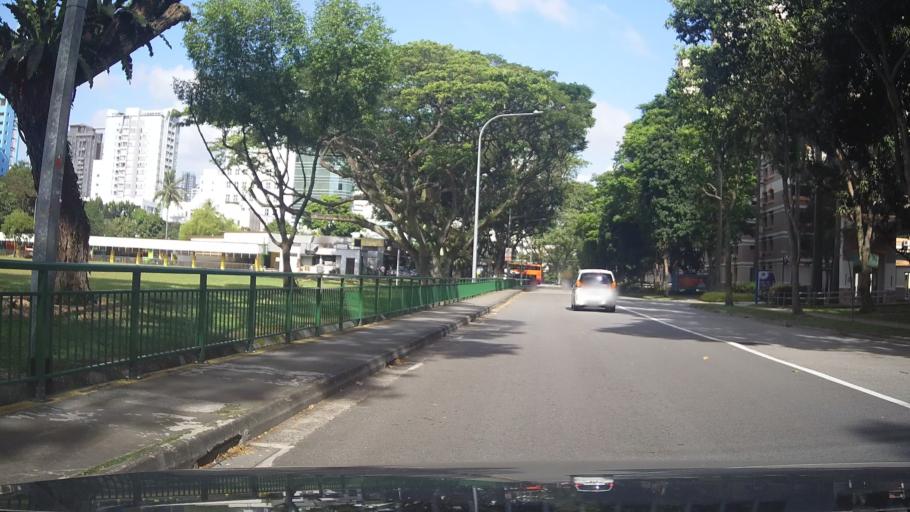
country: SG
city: Singapore
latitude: 1.3256
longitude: 103.8566
